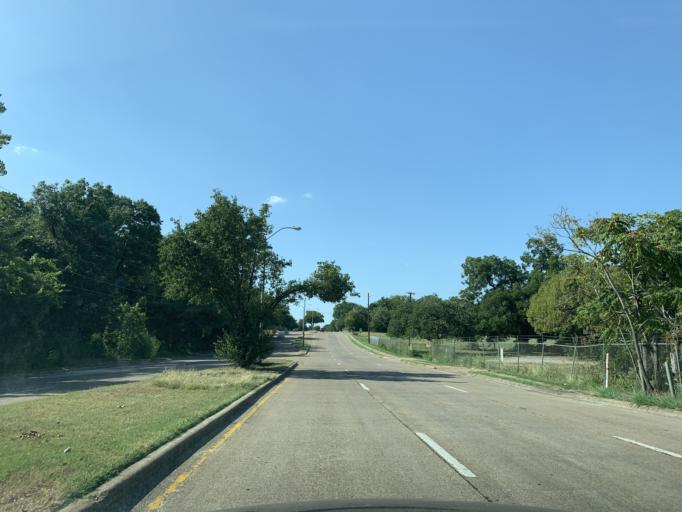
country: US
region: Texas
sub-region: Dallas County
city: Hutchins
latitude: 32.6871
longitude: -96.7697
